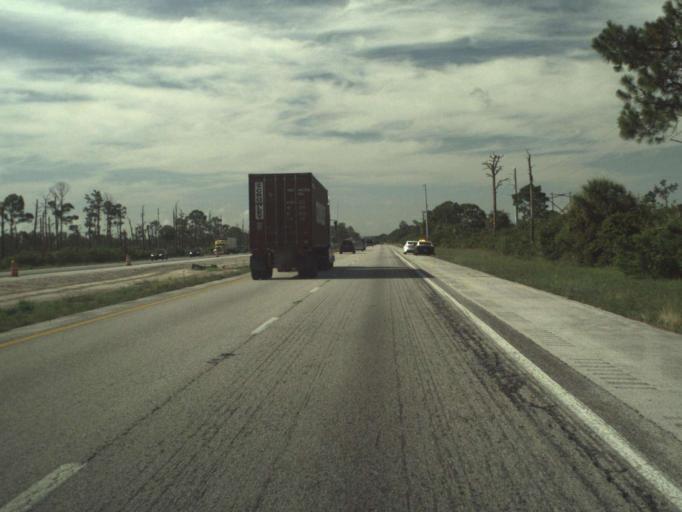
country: US
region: Florida
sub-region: Indian River County
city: West Vero Corridor
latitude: 27.6749
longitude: -80.5322
